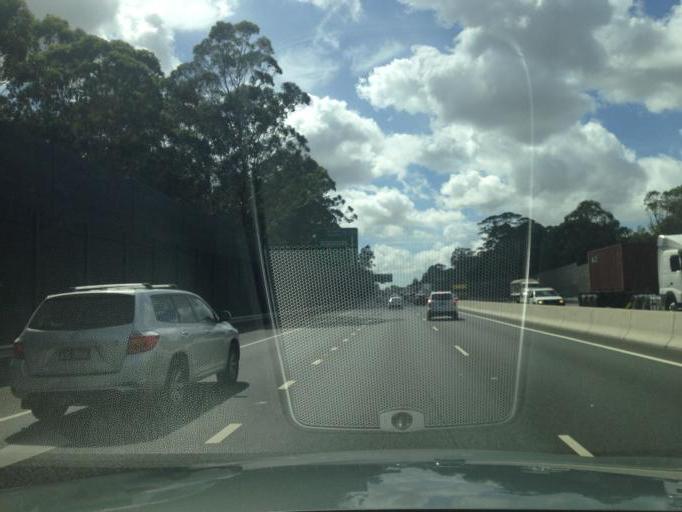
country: AU
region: New South Wales
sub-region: Canterbury
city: Roselands
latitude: -33.9436
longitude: 151.0655
